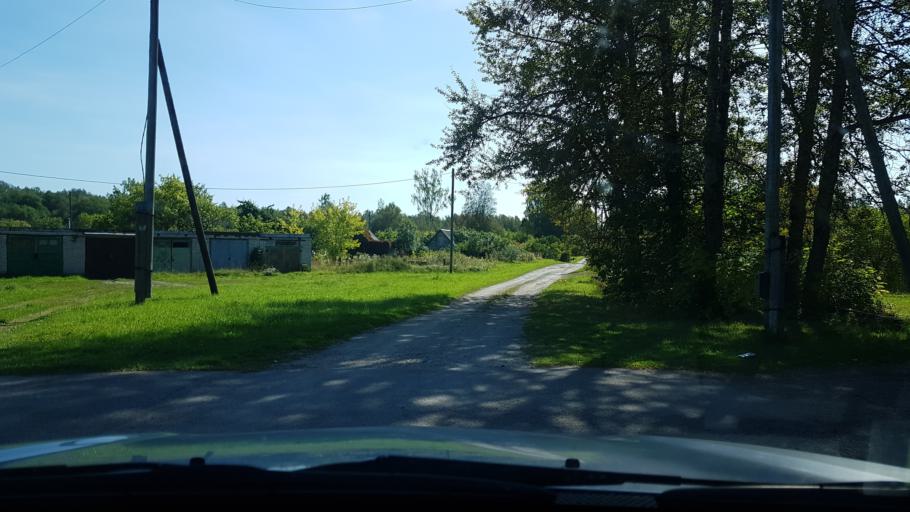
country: EE
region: Ida-Virumaa
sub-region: Sillamaee linn
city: Sillamae
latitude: 59.3199
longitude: 27.7813
